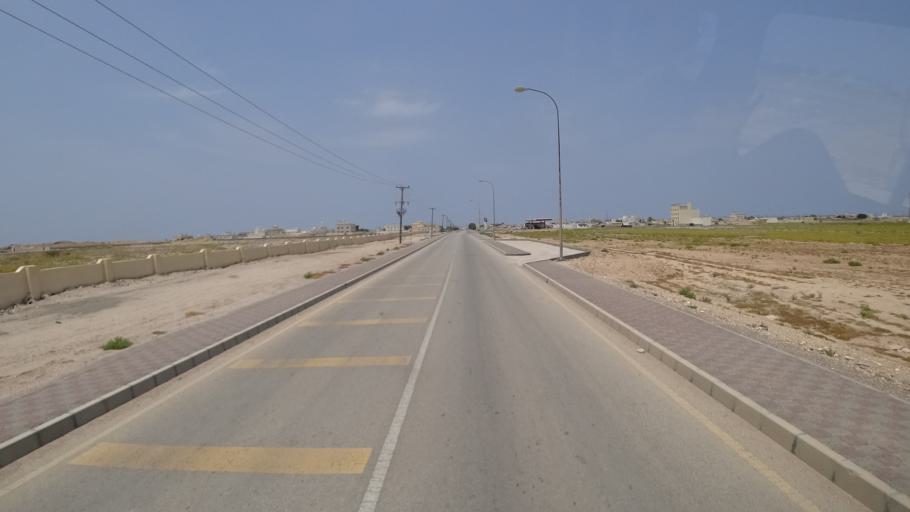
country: OM
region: Ash Sharqiyah
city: Sur
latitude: 22.5106
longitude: 59.7942
